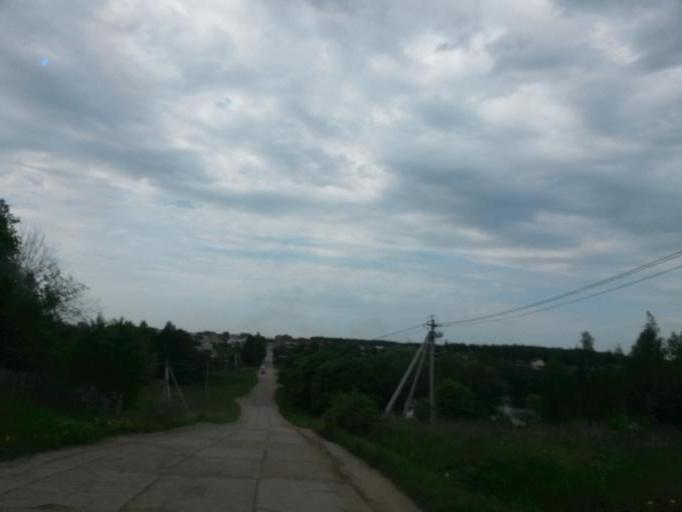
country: RU
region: Moskovskaya
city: Melikhovo
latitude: 55.1512
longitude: 37.6331
